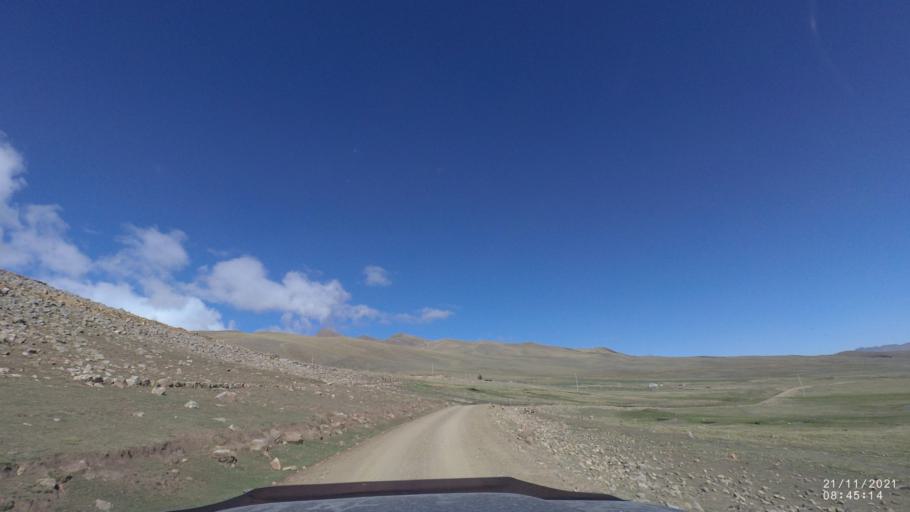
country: BO
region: Cochabamba
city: Cochabamba
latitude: -17.2497
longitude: -66.2309
